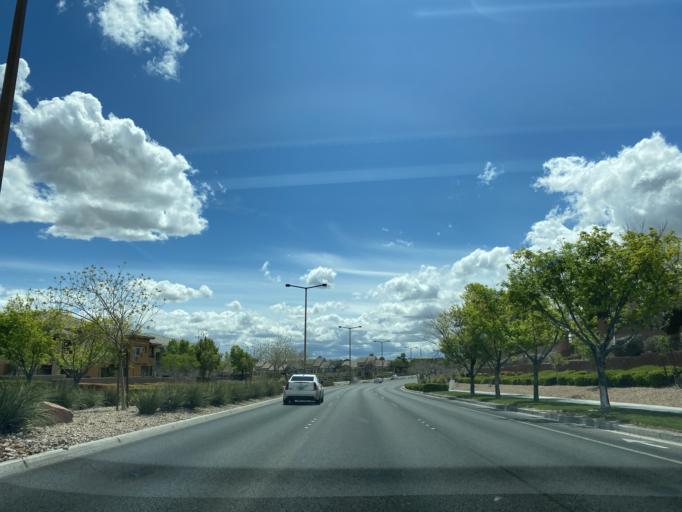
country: US
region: Nevada
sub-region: Clark County
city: Summerlin South
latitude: 36.1649
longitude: -115.3239
